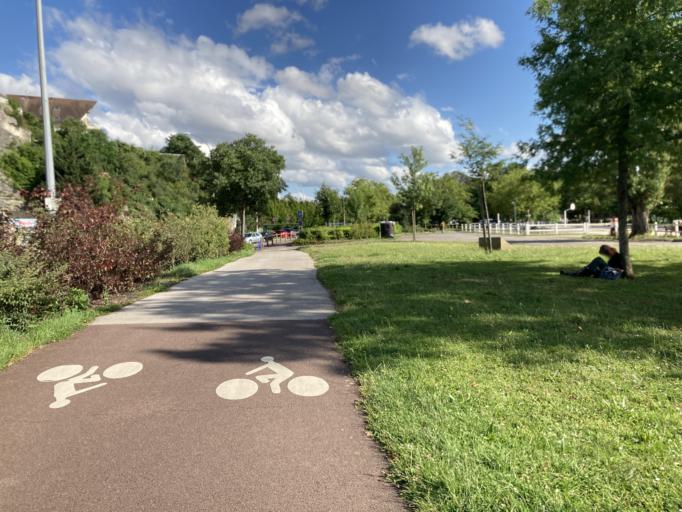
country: FR
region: Bourgogne
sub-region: Departement de la Cote-d'Or
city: Talant
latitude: 47.3255
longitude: 5.0074
